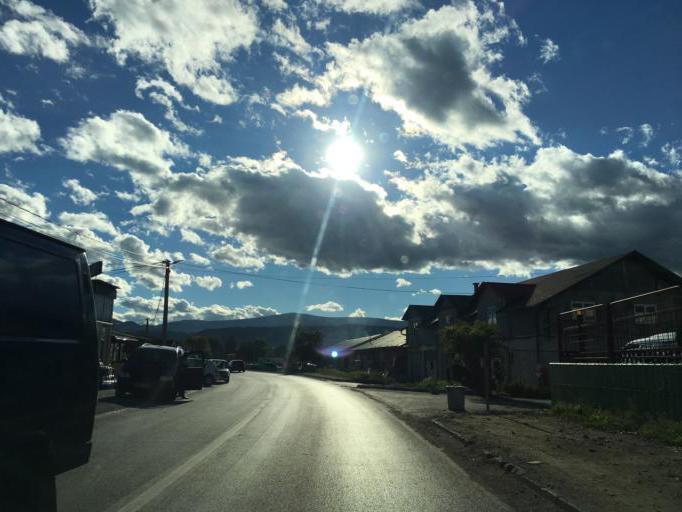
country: BA
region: Federation of Bosnia and Herzegovina
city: Bugojno
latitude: 44.0587
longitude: 17.4611
